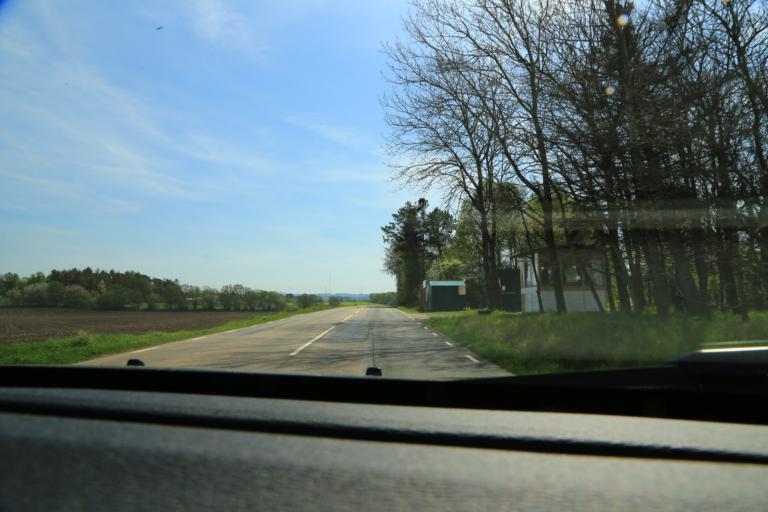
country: SE
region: Halland
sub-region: Varbergs Kommun
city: Varberg
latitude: 57.1342
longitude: 12.3159
